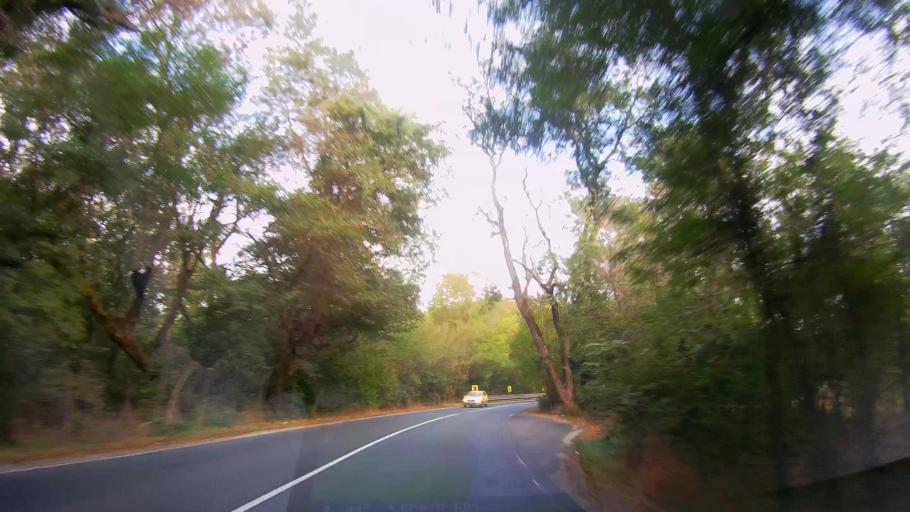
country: BG
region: Burgas
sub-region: Obshtina Primorsko
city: Primorsko
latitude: 42.3041
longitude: 27.7230
